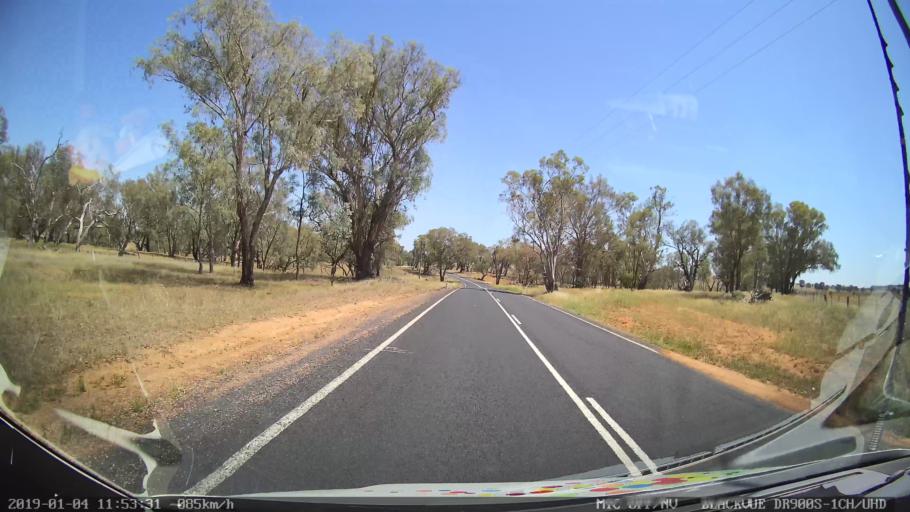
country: AU
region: New South Wales
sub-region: Cabonne
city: Molong
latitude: -32.8744
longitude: 148.7394
